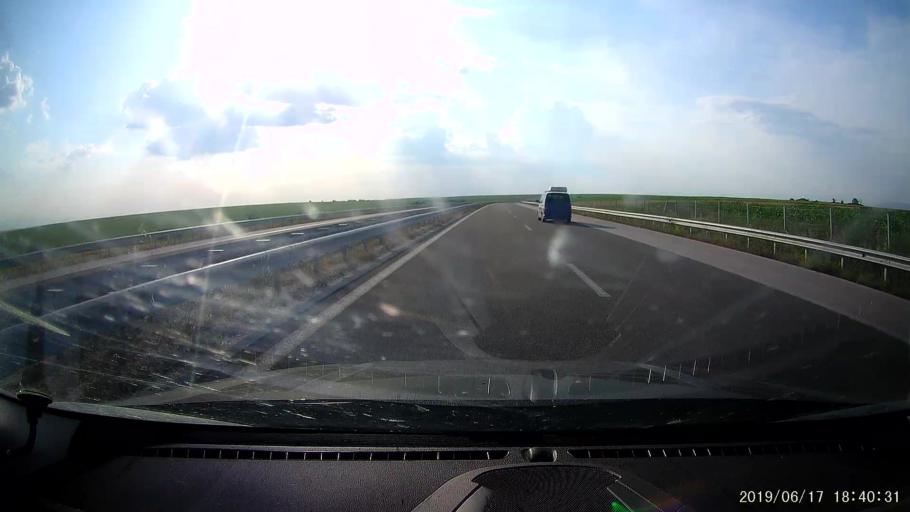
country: BG
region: Stara Zagora
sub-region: Obshtina Chirpan
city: Chirpan
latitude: 42.1565
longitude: 25.2760
